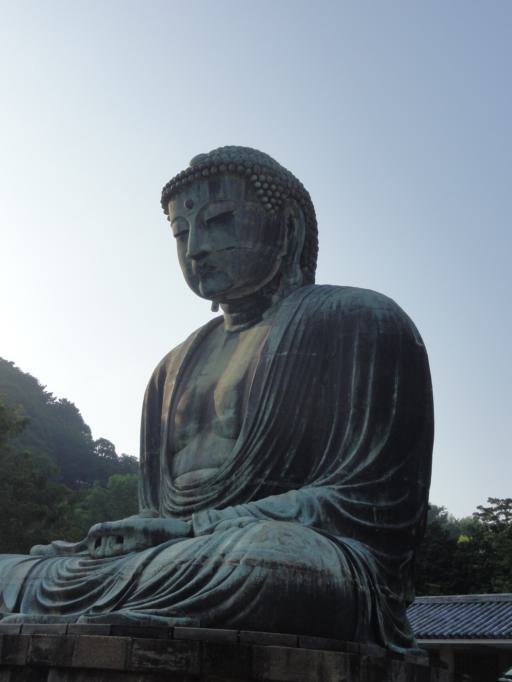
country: JP
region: Kanagawa
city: Kamakura
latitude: 35.3166
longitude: 139.5358
